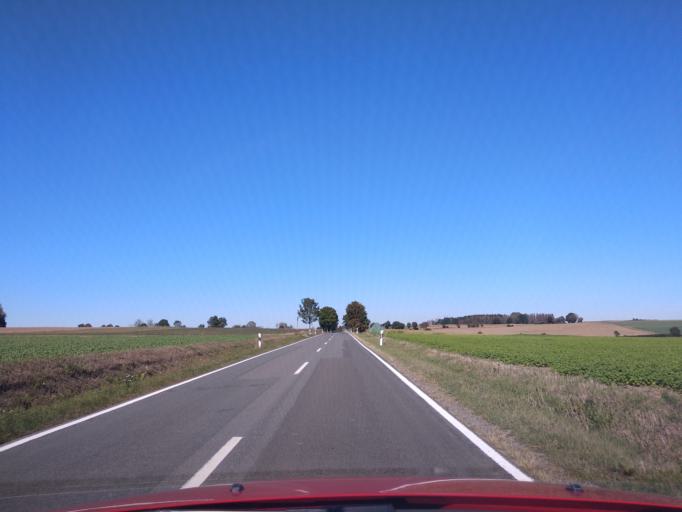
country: DE
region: Lower Saxony
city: Boffzen
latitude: 51.7344
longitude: 9.2977
